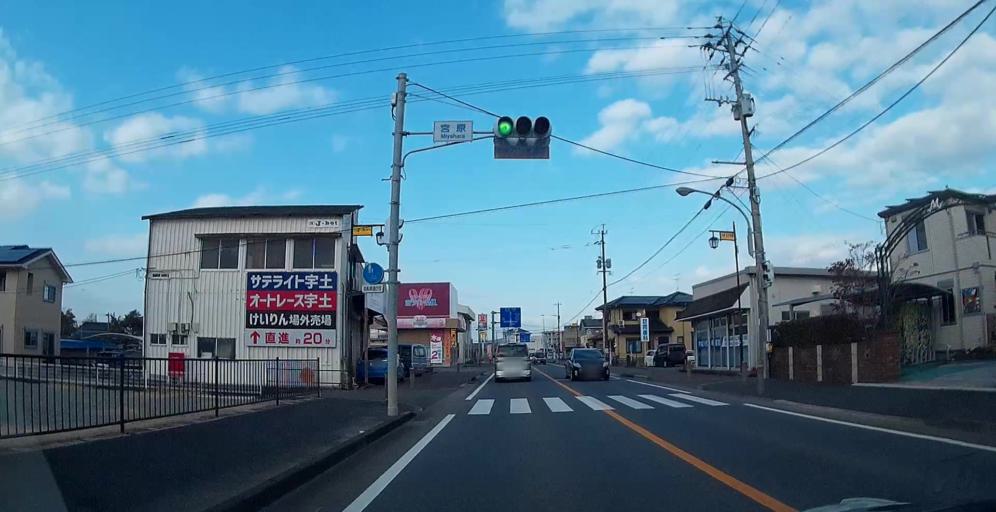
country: JP
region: Kumamoto
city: Yatsushiro
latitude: 32.5555
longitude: 130.6807
